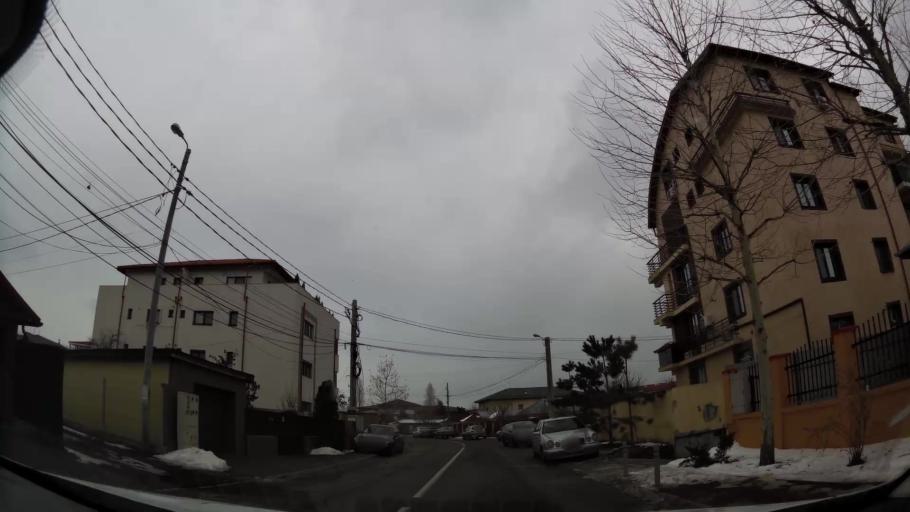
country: RO
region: Ilfov
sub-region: Comuna Otopeni
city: Otopeni
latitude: 44.5542
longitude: 26.0762
